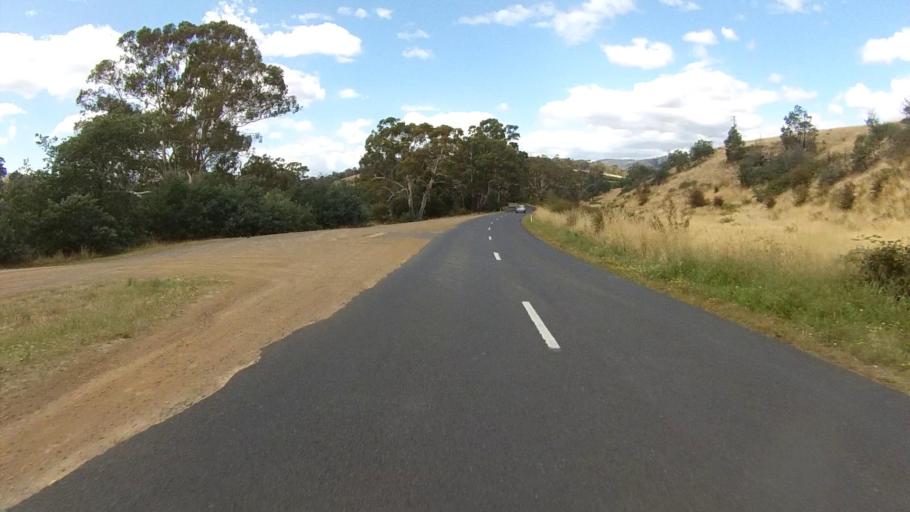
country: AU
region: Tasmania
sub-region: Derwent Valley
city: New Norfolk
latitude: -42.7554
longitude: 146.9850
